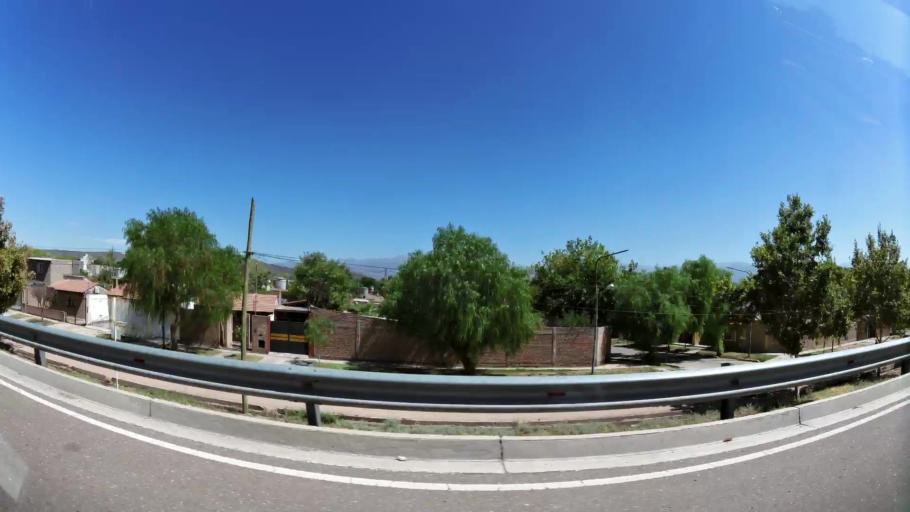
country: AR
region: Mendoza
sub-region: Departamento de Godoy Cruz
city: Godoy Cruz
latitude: -32.9301
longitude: -68.8643
